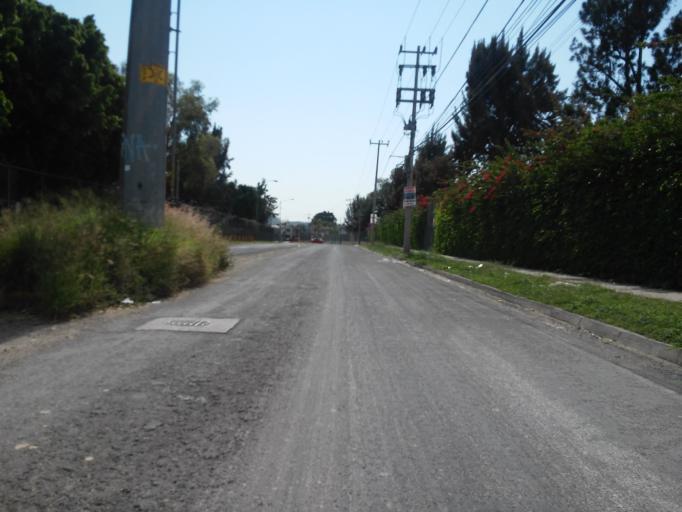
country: MX
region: Jalisco
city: Guadalajara
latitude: 20.6464
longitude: -103.4177
